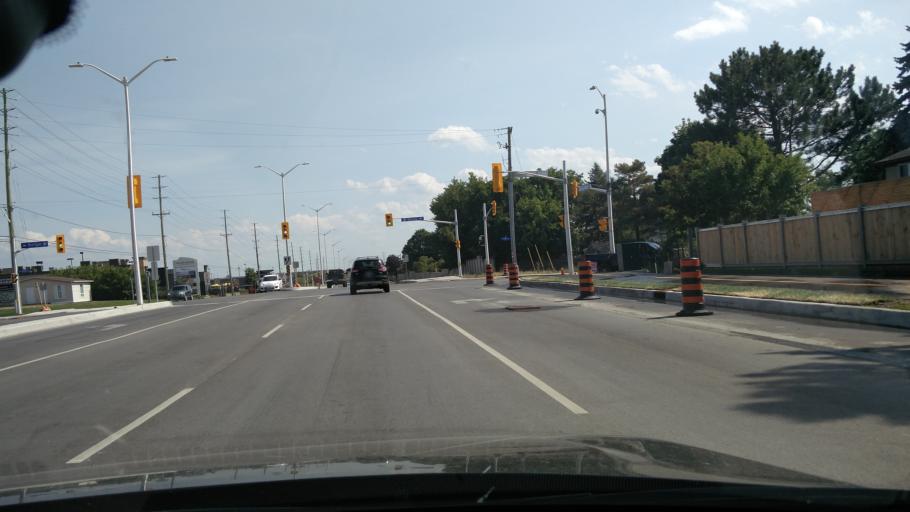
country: CA
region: Ontario
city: Bells Corners
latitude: 45.2754
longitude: -75.7494
